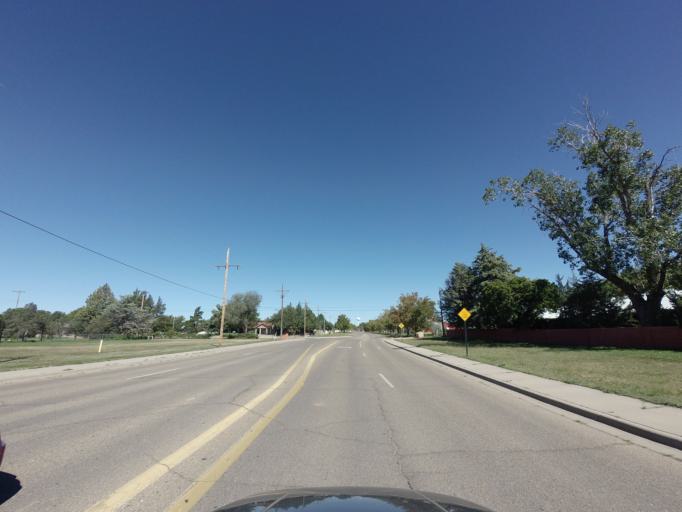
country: US
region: New Mexico
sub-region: Curry County
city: Clovis
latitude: 34.4197
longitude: -103.1876
